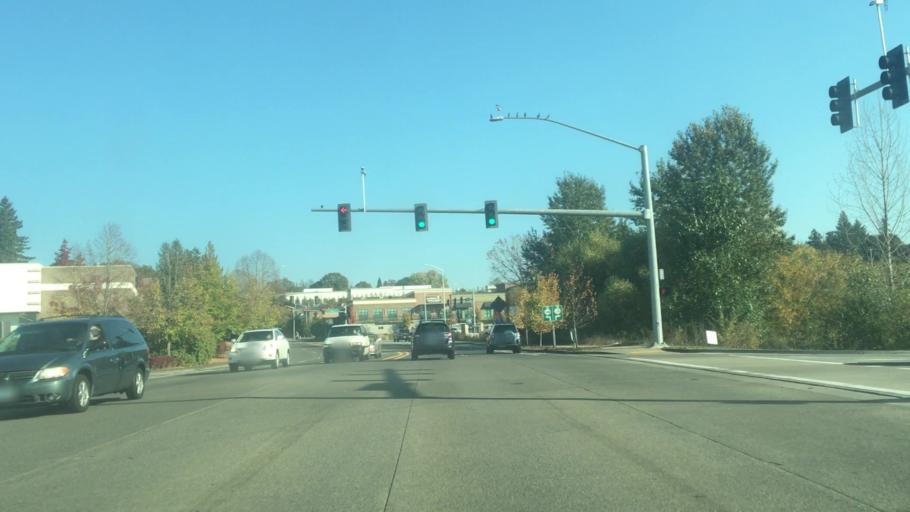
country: US
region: Oregon
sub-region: Washington County
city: Metzger
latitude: 45.4333
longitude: -122.7531
